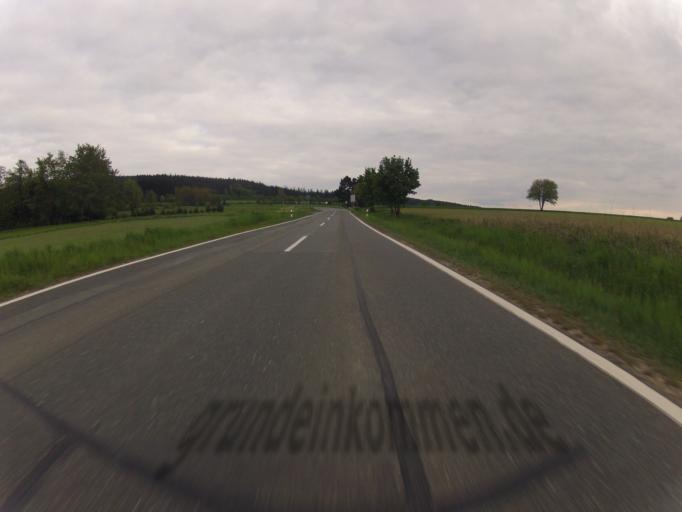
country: DE
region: Bavaria
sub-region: Upper Franconia
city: Sparneck
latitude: 50.1558
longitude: 11.8497
